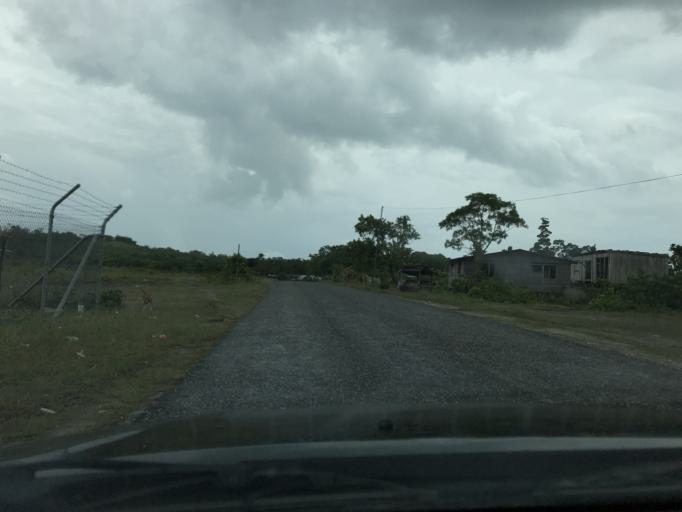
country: SB
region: Western Province
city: Gizo
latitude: -8.3268
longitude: 157.2714
